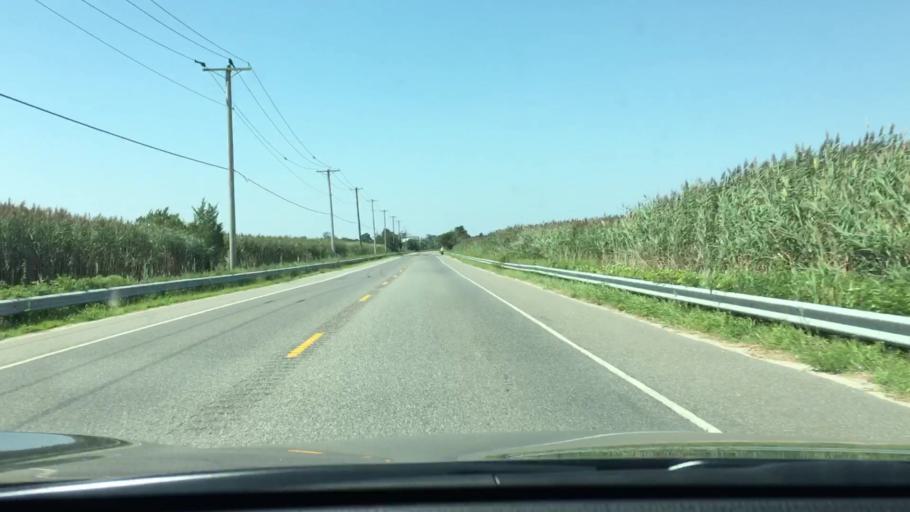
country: US
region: New Jersey
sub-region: Cumberland County
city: Port Norris
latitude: 39.2877
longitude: -74.9805
